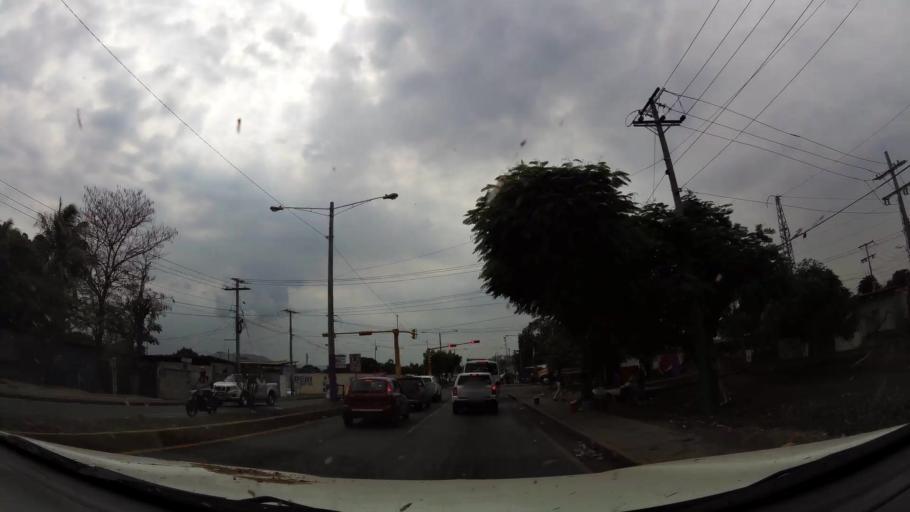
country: NI
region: Masaya
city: Masaya
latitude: 11.9817
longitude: -86.0864
